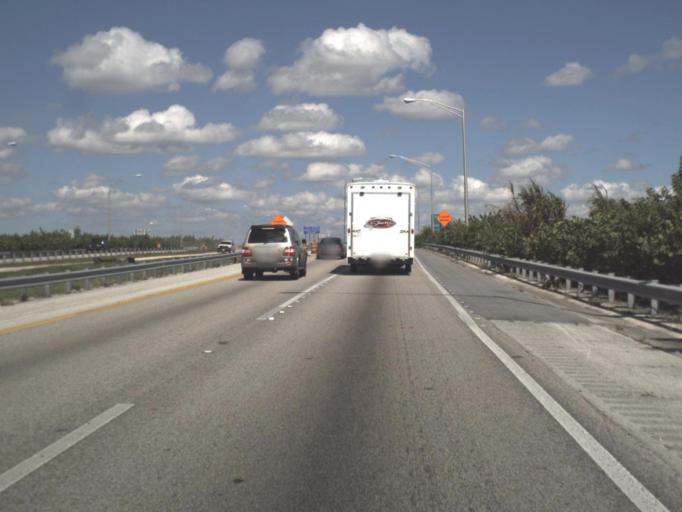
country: US
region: Florida
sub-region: Miami-Dade County
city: Goulds
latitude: 25.5638
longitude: -80.3628
